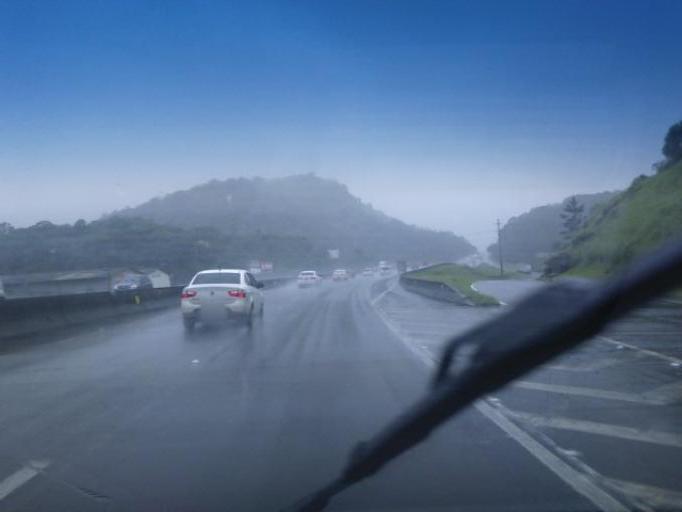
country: BR
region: Santa Catarina
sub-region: Joinville
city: Joinville
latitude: -26.2332
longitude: -48.9165
